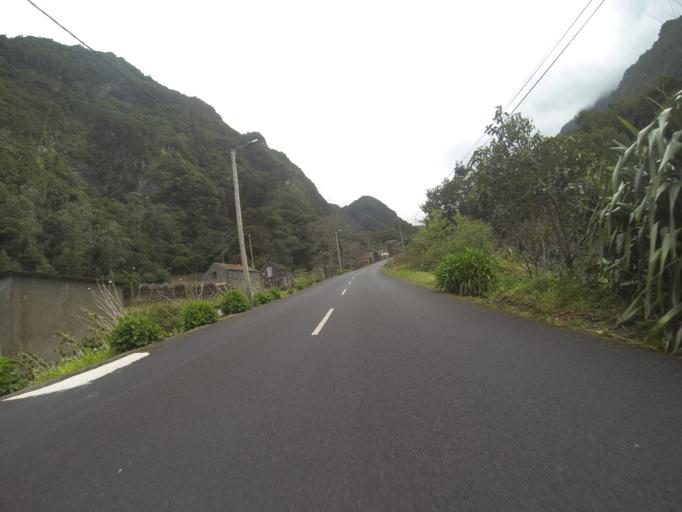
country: PT
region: Madeira
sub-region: Porto Moniz
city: Porto Moniz
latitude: 32.8160
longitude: -17.1094
